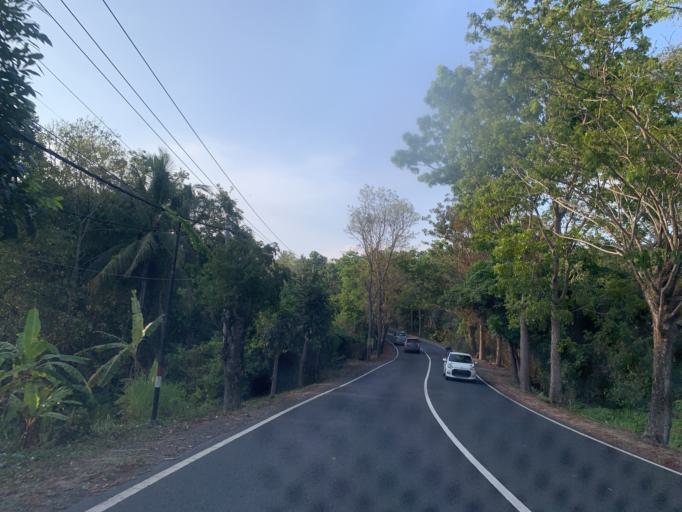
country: ID
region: Bali
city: Banjar Delodrurung
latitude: -8.5021
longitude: 114.9719
